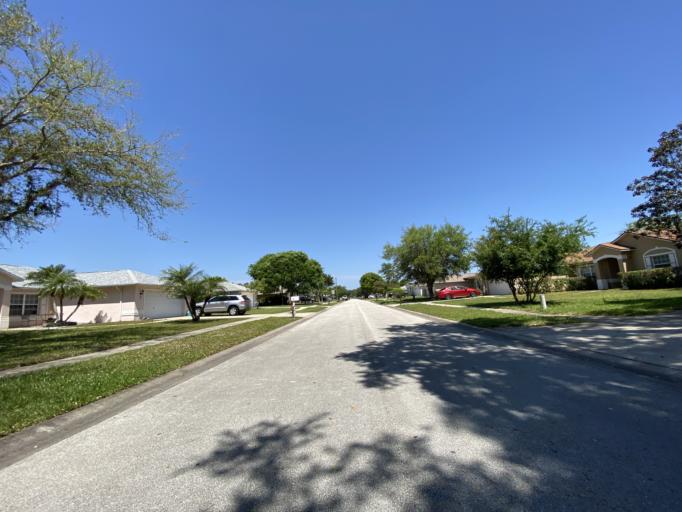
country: US
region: Florida
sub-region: Volusia County
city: Port Orange
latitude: 29.1503
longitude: -81.0039
